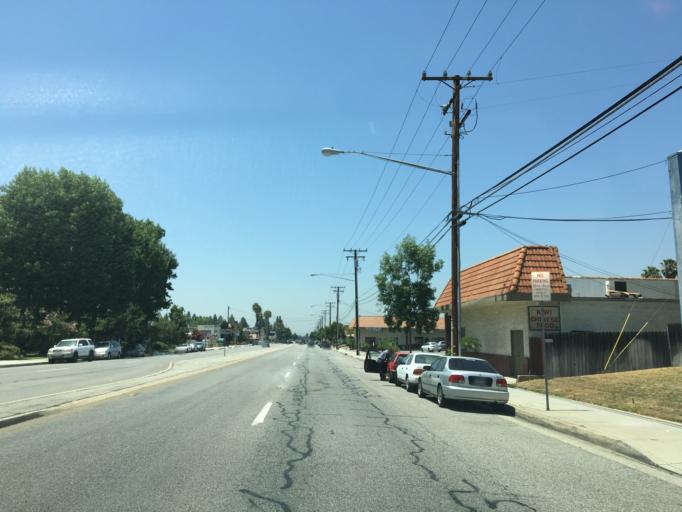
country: US
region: California
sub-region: Los Angeles County
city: Charter Oak
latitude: 34.1068
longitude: -117.8506
